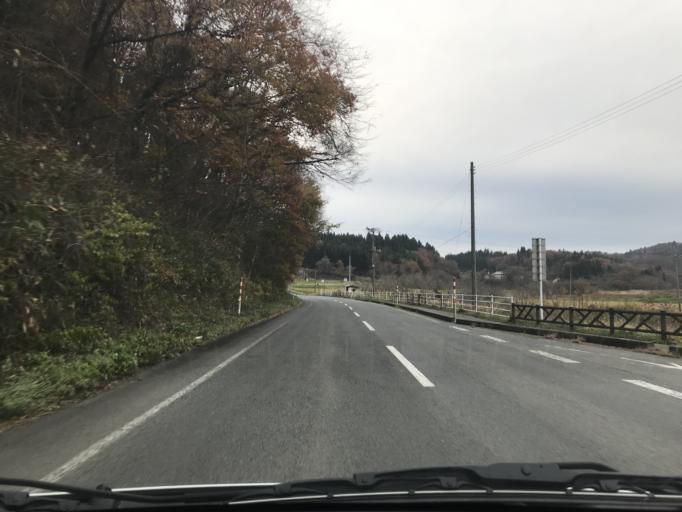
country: JP
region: Iwate
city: Kitakami
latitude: 39.2656
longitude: 141.2682
